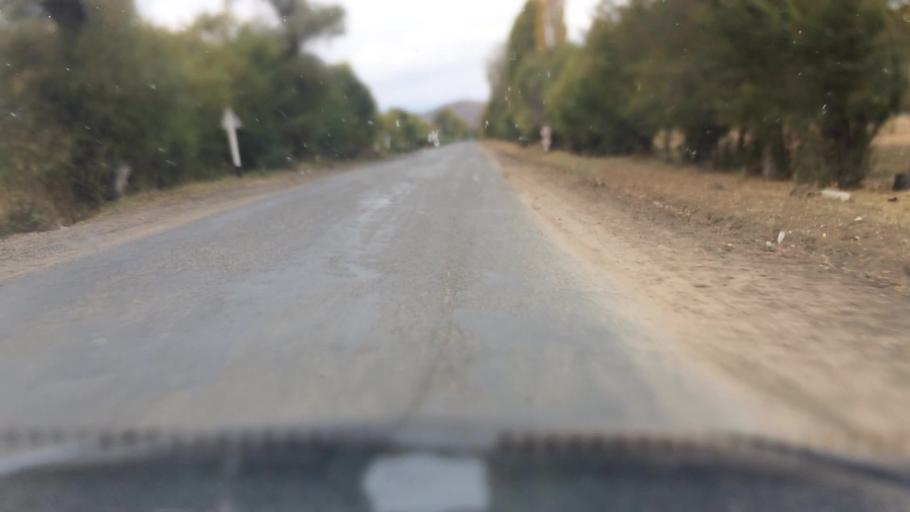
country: KG
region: Ysyk-Koel
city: Pokrovka
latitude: 42.7371
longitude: 77.9310
